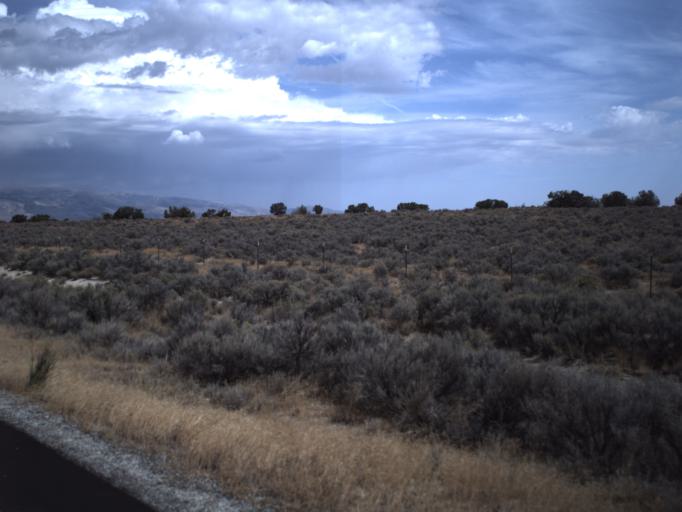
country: US
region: Idaho
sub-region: Cassia County
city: Burley
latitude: 41.7050
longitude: -113.5321
